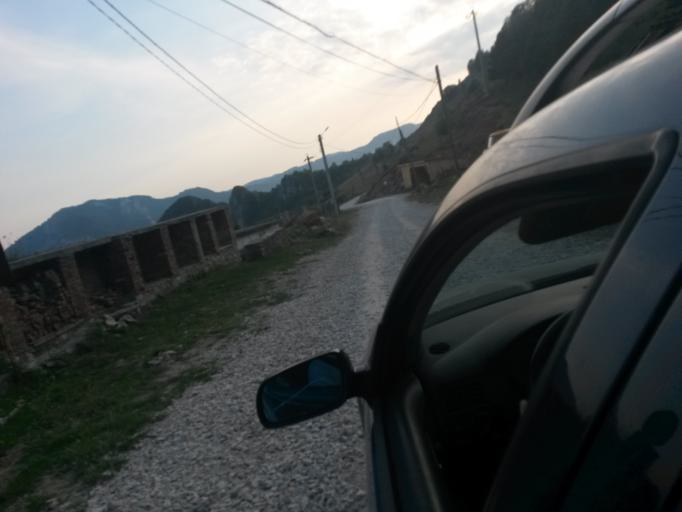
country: RO
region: Alba
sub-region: Comuna Ponor
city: Ponor
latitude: 46.3163
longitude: 23.5239
